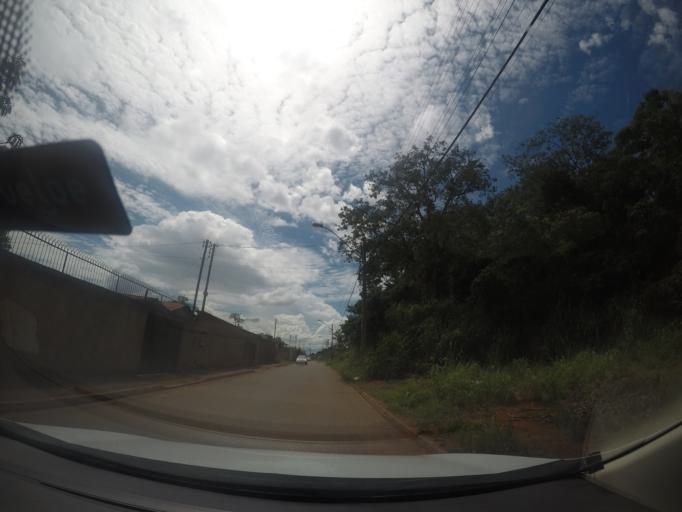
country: BR
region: Goias
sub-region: Goiania
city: Goiania
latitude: -16.6612
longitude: -49.3452
